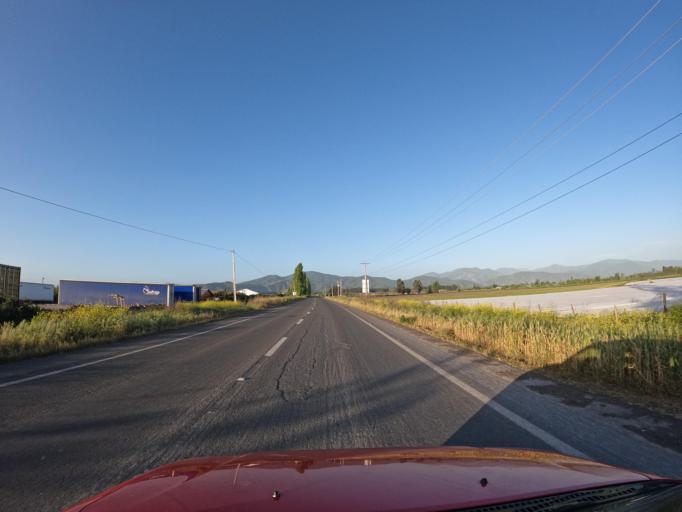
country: CL
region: O'Higgins
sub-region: Provincia de Cachapoal
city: San Vicente
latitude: -34.2995
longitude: -71.3742
